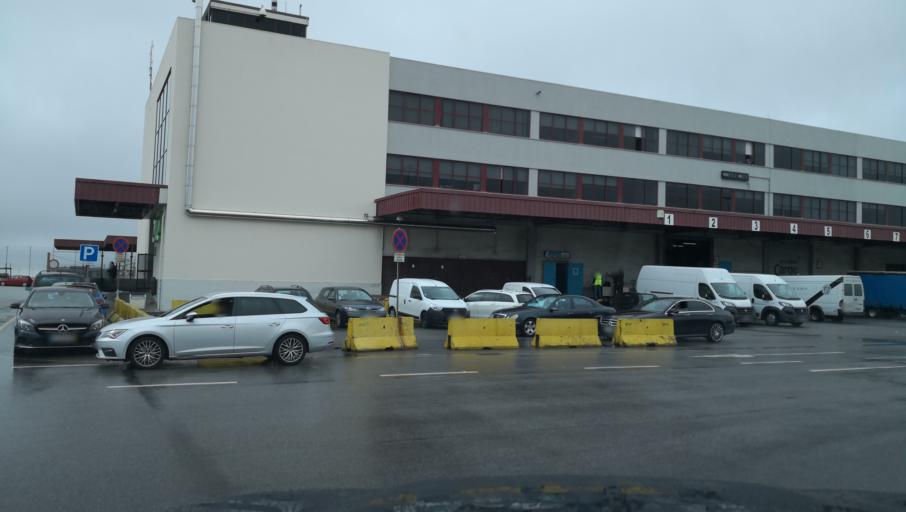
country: PT
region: Porto
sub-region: Matosinhos
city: Santa Cruz do Bispo
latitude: 41.2406
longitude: -8.6711
